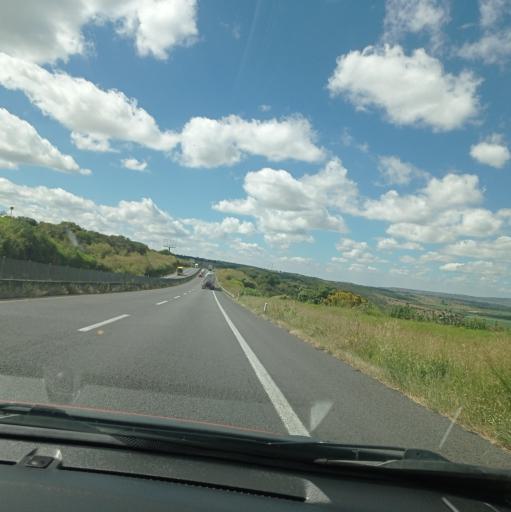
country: MX
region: Jalisco
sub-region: Acatic
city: Tierras Coloradas
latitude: 20.7711
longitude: -102.8452
